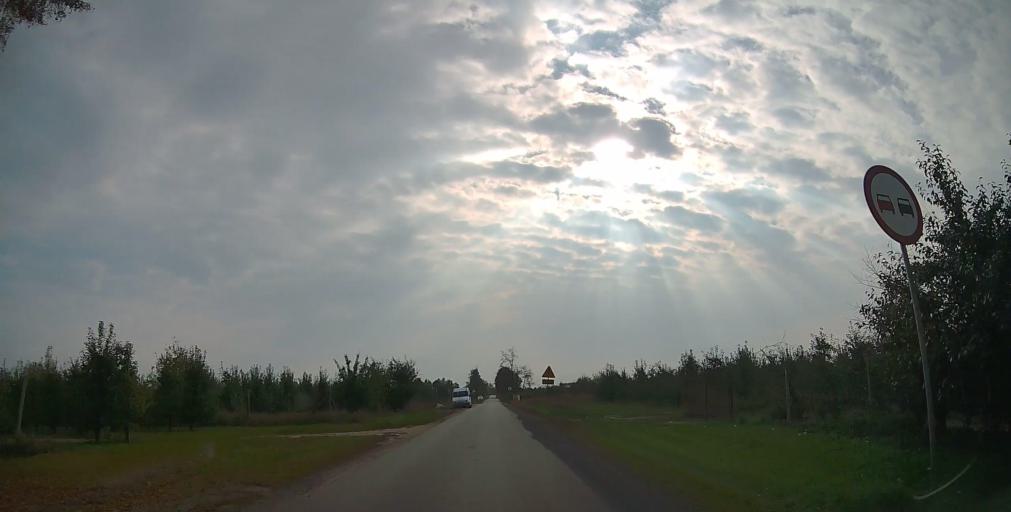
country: PL
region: Masovian Voivodeship
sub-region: Powiat grojecki
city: Mogielnica
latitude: 51.6500
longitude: 20.7283
